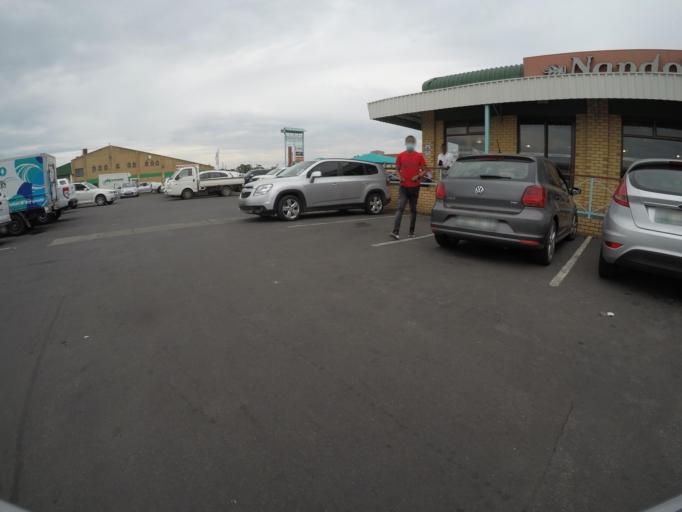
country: ZA
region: Eastern Cape
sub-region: Buffalo City Metropolitan Municipality
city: East London
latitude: -32.9832
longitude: 27.8995
